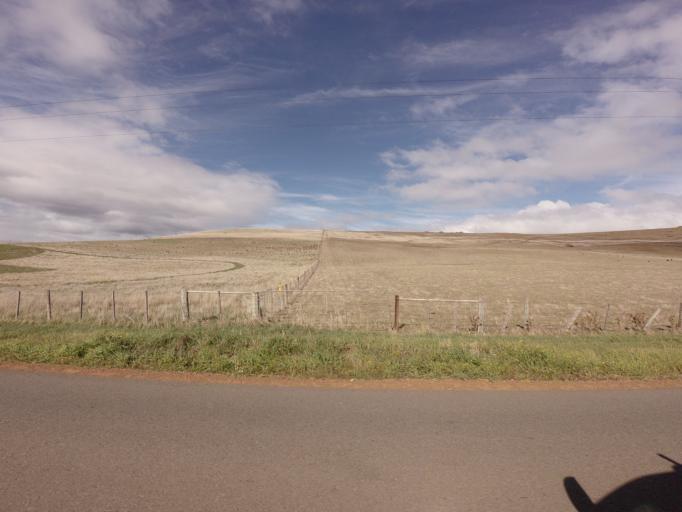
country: AU
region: Tasmania
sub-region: Derwent Valley
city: New Norfolk
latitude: -42.6950
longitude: 146.9331
